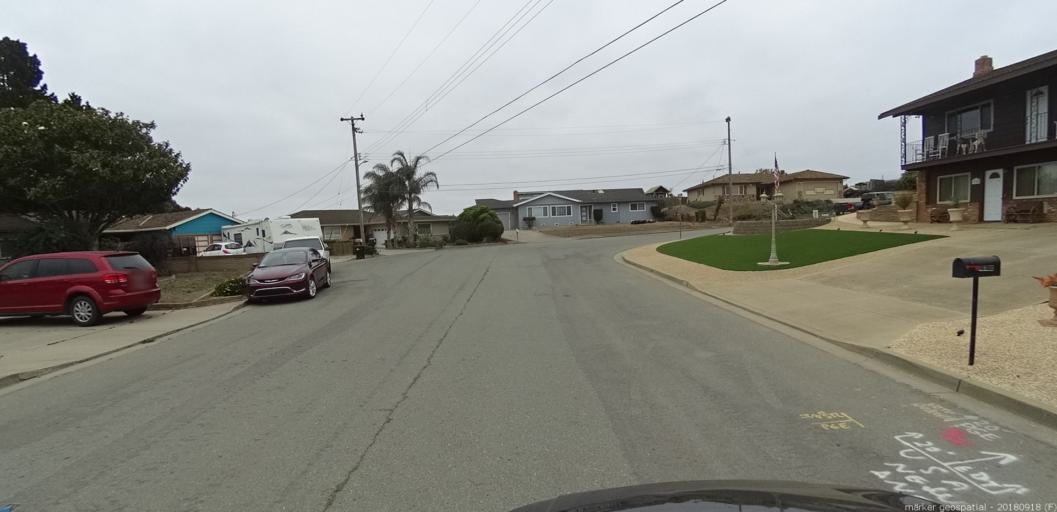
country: US
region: California
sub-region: Monterey County
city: Boronda
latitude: 36.7341
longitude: -121.6432
